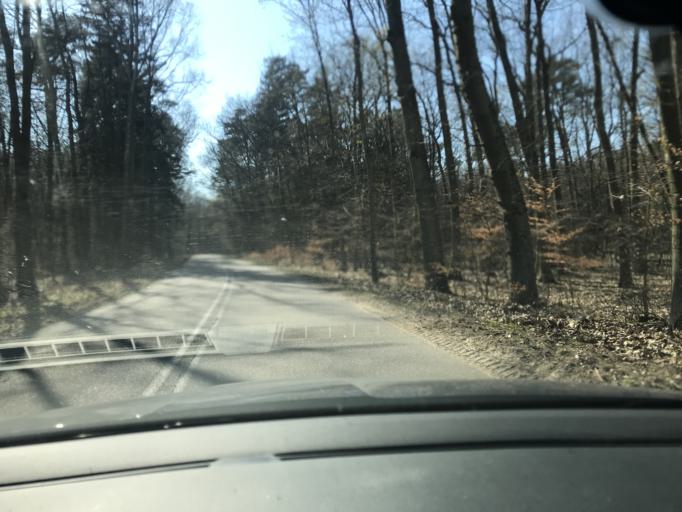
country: PL
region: Pomeranian Voivodeship
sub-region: Powiat nowodworski
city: Krynica Morska
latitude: 54.3681
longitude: 19.3977
